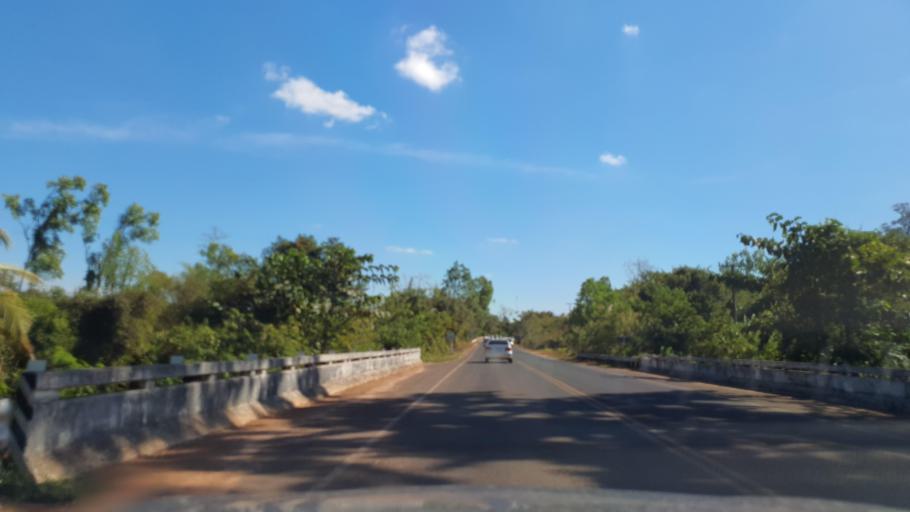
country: TH
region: Kalasin
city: Khao Wong
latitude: 16.7775
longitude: 104.1512
